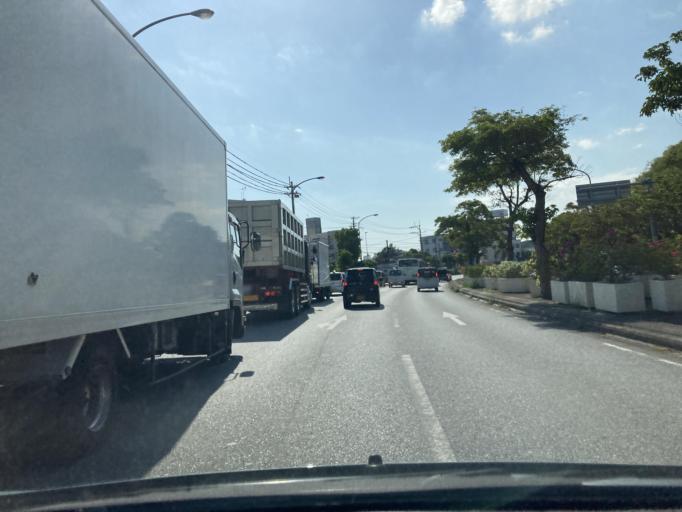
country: JP
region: Okinawa
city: Chatan
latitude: 26.2966
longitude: 127.7855
